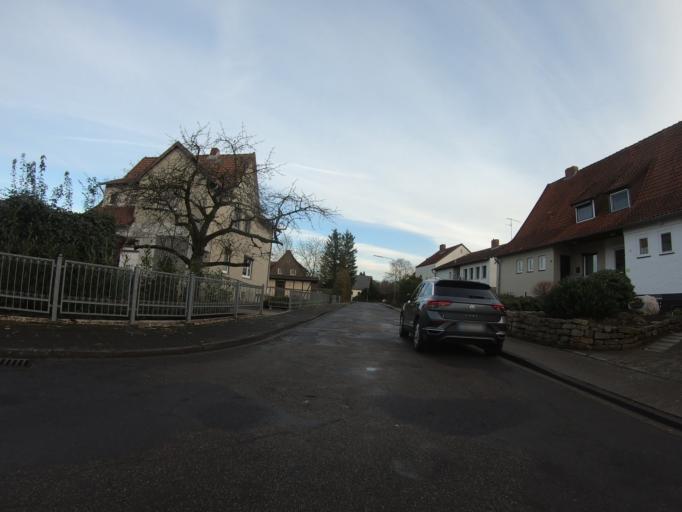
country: DE
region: Lower Saxony
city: Gifhorn
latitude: 52.4708
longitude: 10.5396
